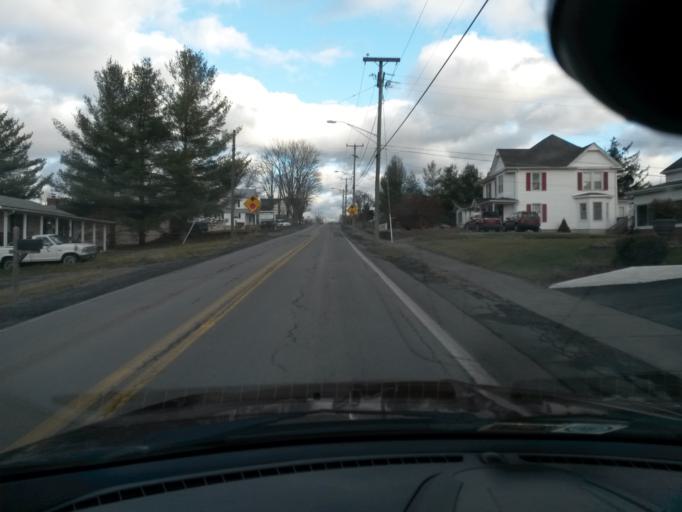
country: US
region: West Virginia
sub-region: Monroe County
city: Union
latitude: 37.5895
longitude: -80.5457
